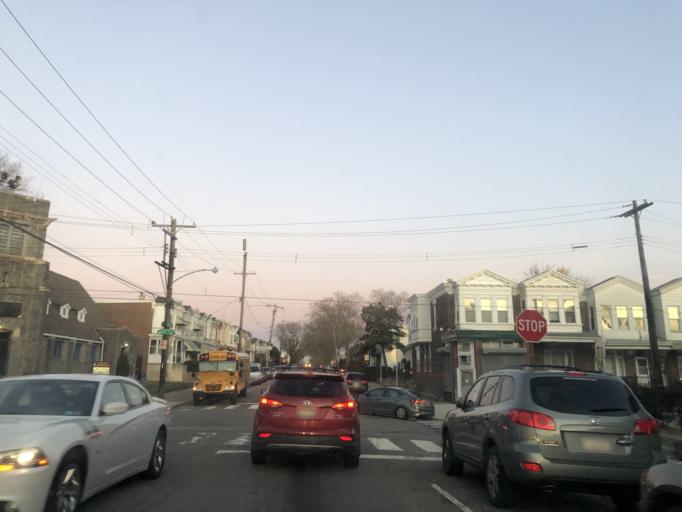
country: US
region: Pennsylvania
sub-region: Delaware County
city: Millbourne
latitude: 39.9787
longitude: -75.2427
